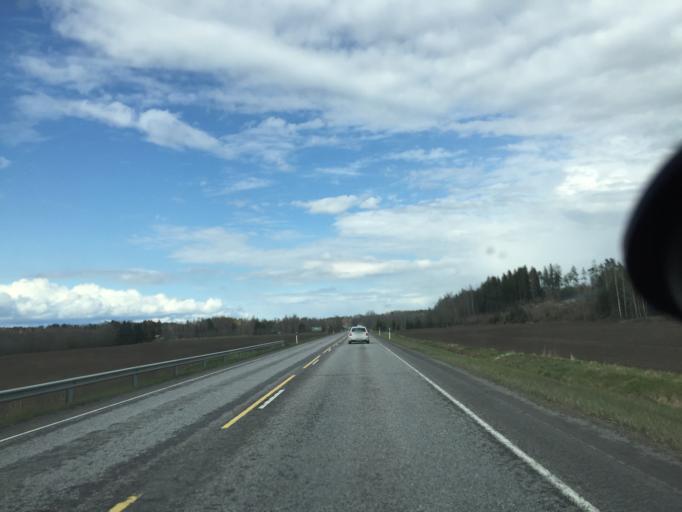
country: FI
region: Uusimaa
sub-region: Helsinki
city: Lohja
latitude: 60.1990
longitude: 24.0133
